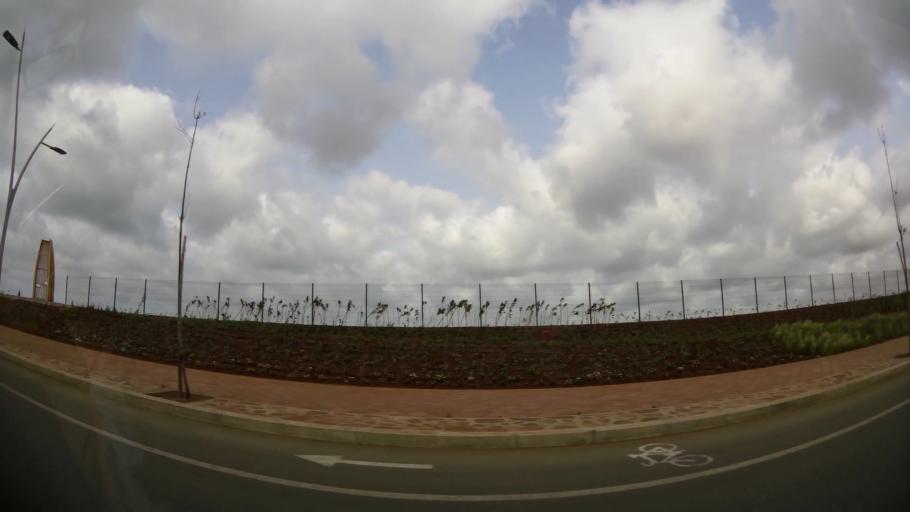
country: MA
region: Oriental
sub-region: Nador
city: Nador
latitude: 35.1599
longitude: -2.9065
